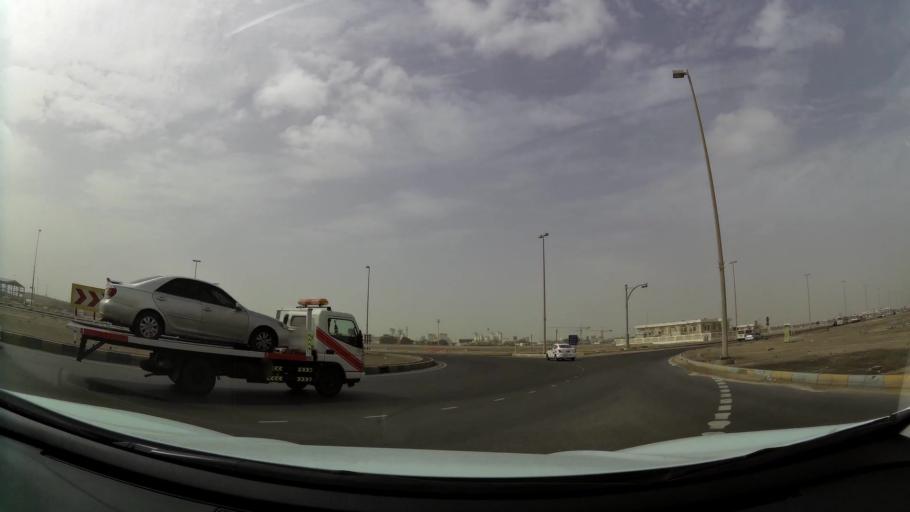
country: AE
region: Abu Dhabi
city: Abu Dhabi
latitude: 24.3375
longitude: 54.5180
